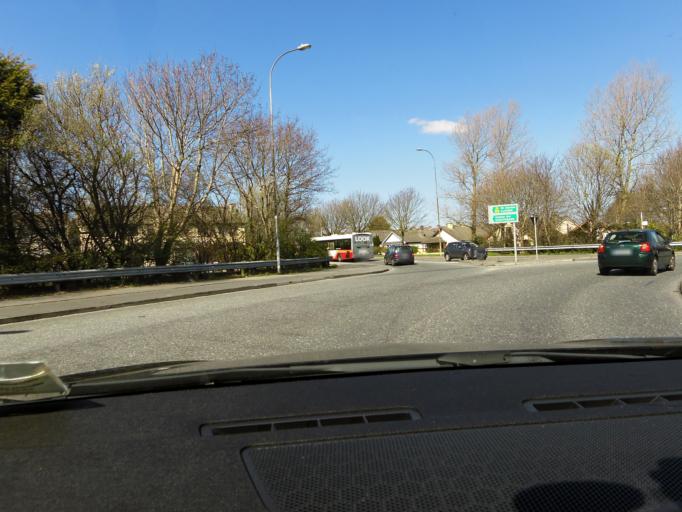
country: IE
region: Connaught
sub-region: County Galway
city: Gaillimh
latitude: 53.2791
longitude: -9.0699
